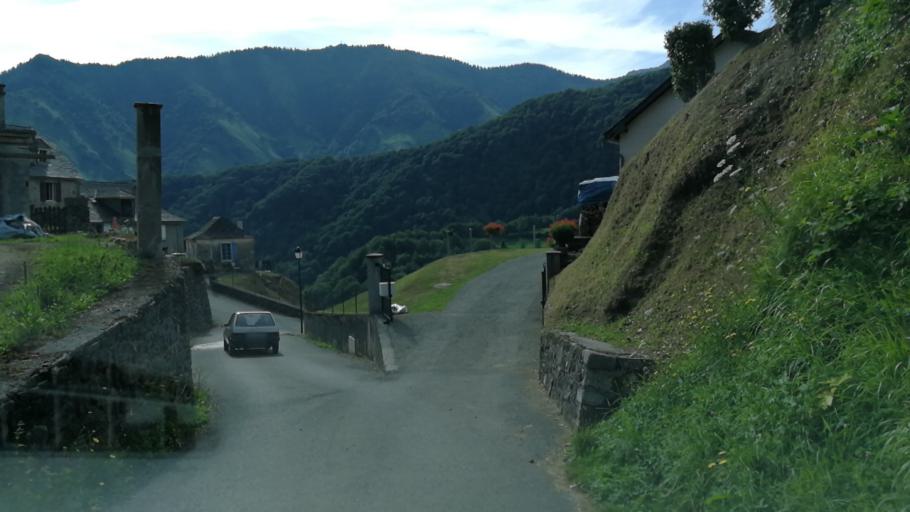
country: FR
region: Aquitaine
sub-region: Departement des Pyrenees-Atlantiques
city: Arette
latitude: 42.9326
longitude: -0.6358
